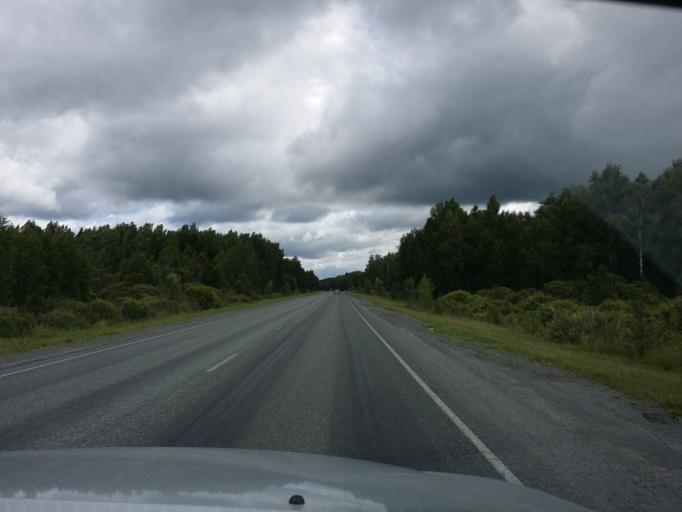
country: RU
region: Tjumen
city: Yarkovo
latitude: 57.6004
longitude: 67.2693
